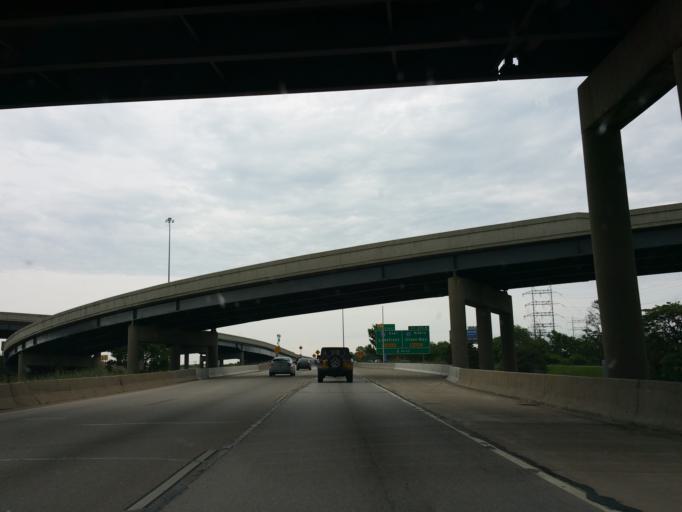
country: US
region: Wisconsin
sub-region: Milwaukee County
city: West Milwaukee
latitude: 43.0327
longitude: -87.9706
